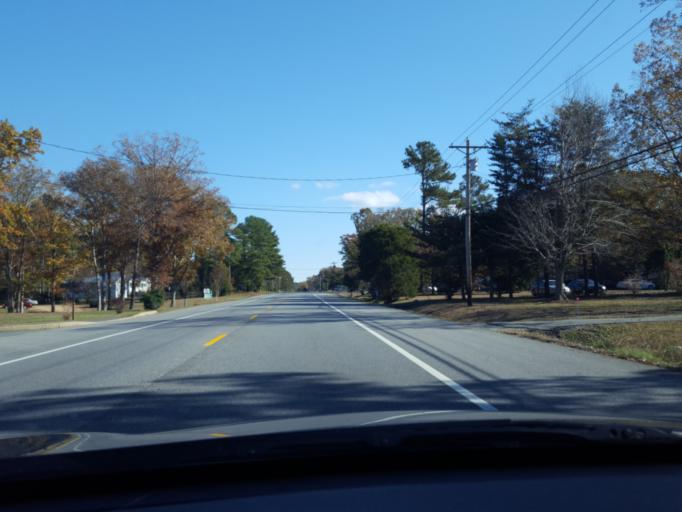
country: US
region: Maryland
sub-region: Saint Mary's County
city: California
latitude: 38.2415
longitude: -76.5613
